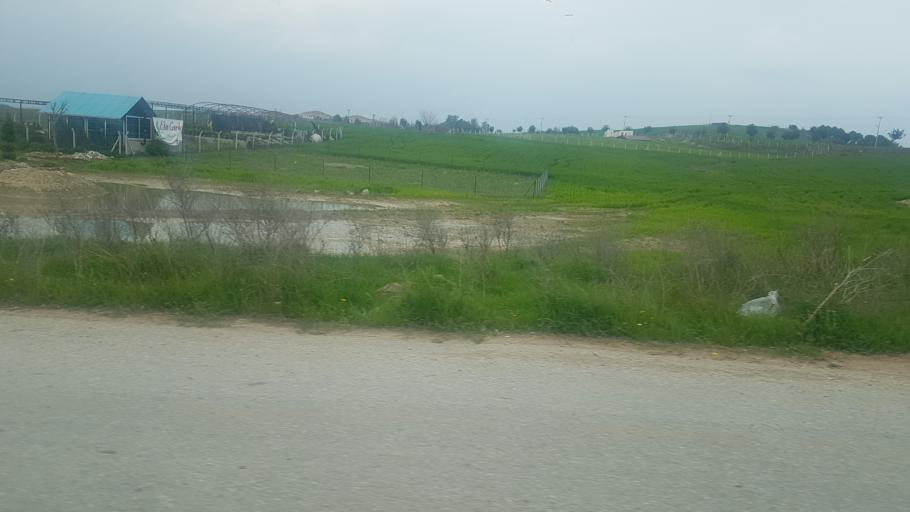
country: TR
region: Adana
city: Seyhan
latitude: 37.0579
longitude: 35.2423
